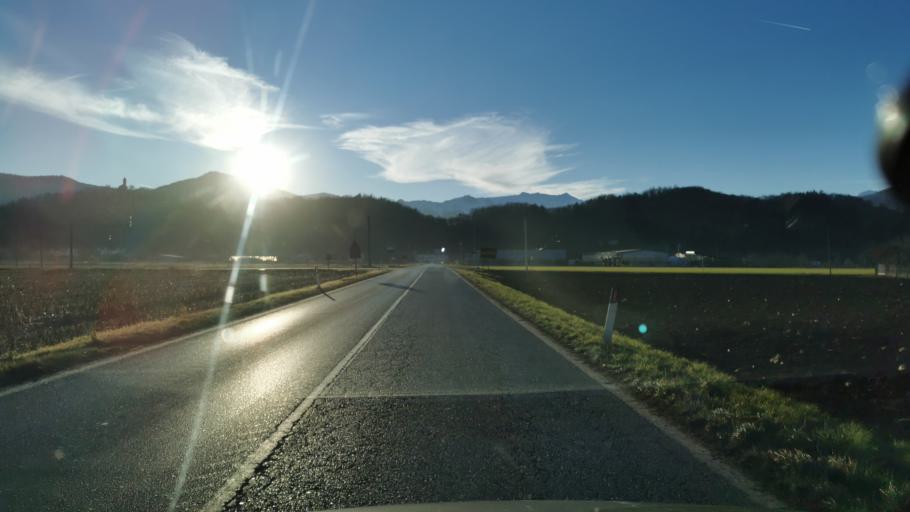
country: IT
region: Piedmont
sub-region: Provincia di Cuneo
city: Caraglio
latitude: 44.4286
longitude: 7.4360
